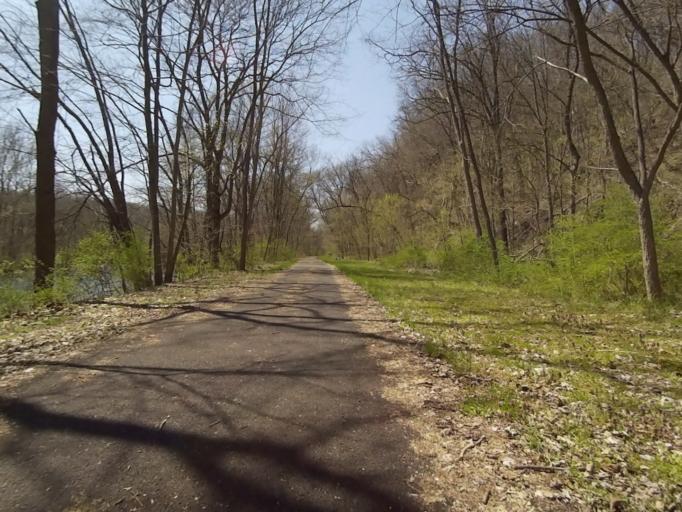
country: US
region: Pennsylvania
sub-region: Blair County
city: Williamsburg
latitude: 40.4787
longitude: -78.1758
